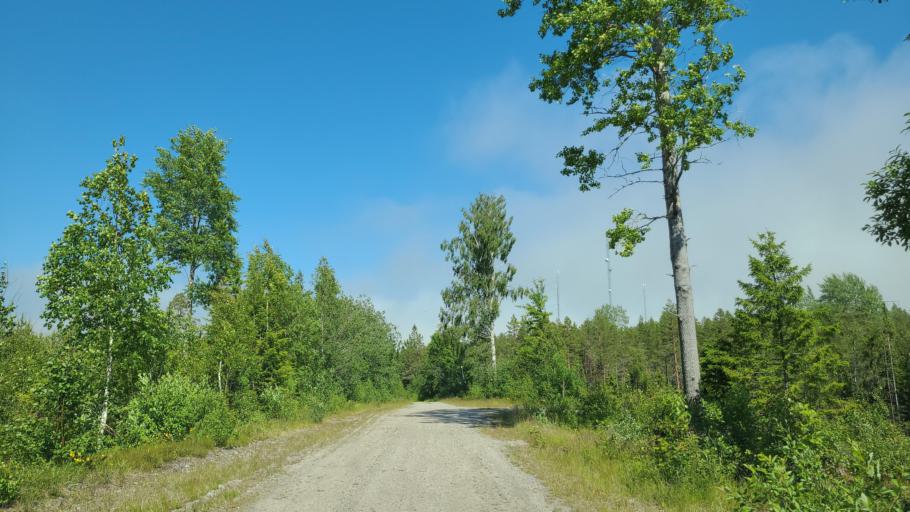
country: SE
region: Vaesternorrland
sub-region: OErnskoeldsviks Kommun
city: Husum
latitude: 63.4448
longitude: 19.2360
